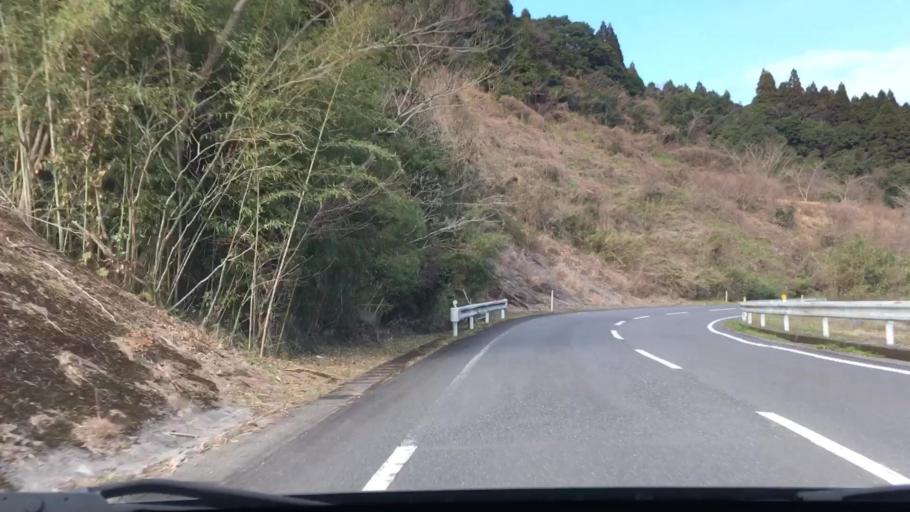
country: JP
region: Miyazaki
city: Kushima
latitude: 31.5700
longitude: 131.2618
